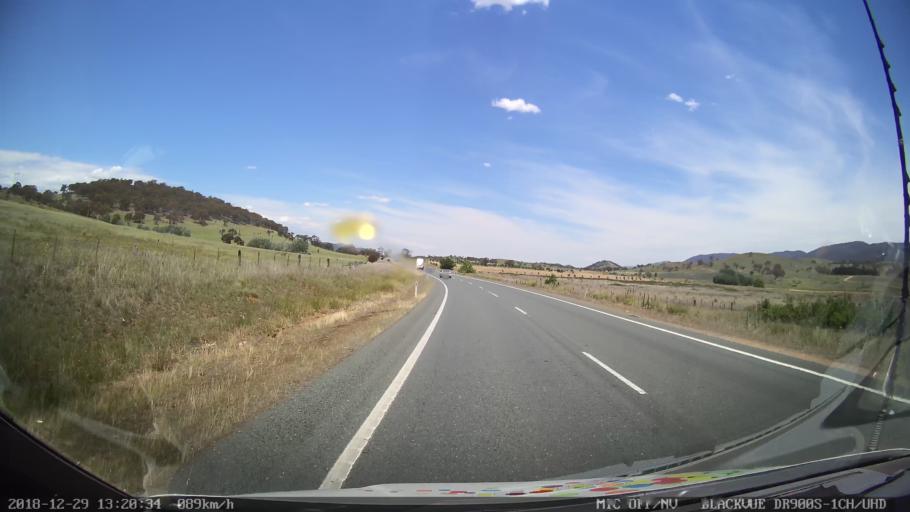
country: AU
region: Australian Capital Territory
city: Macarthur
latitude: -35.7806
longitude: 149.1617
